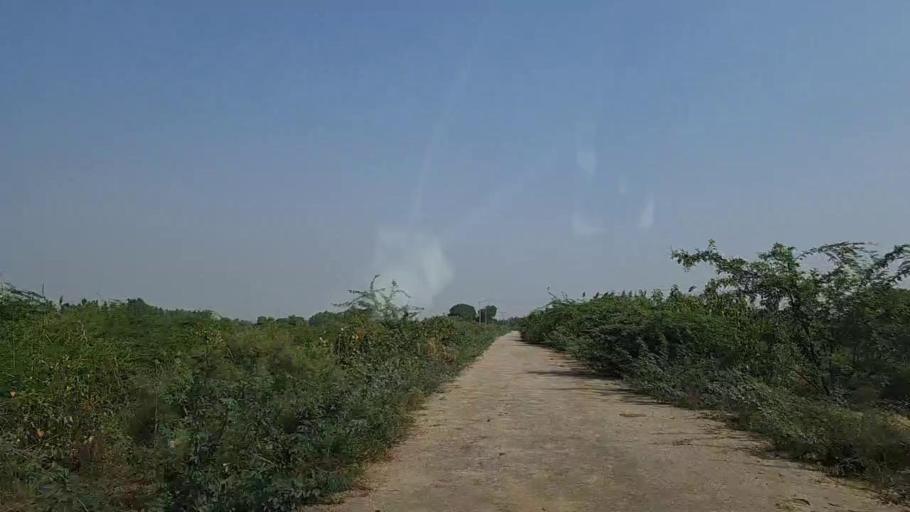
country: PK
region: Sindh
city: Mirpur Sakro
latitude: 24.6508
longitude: 67.6921
